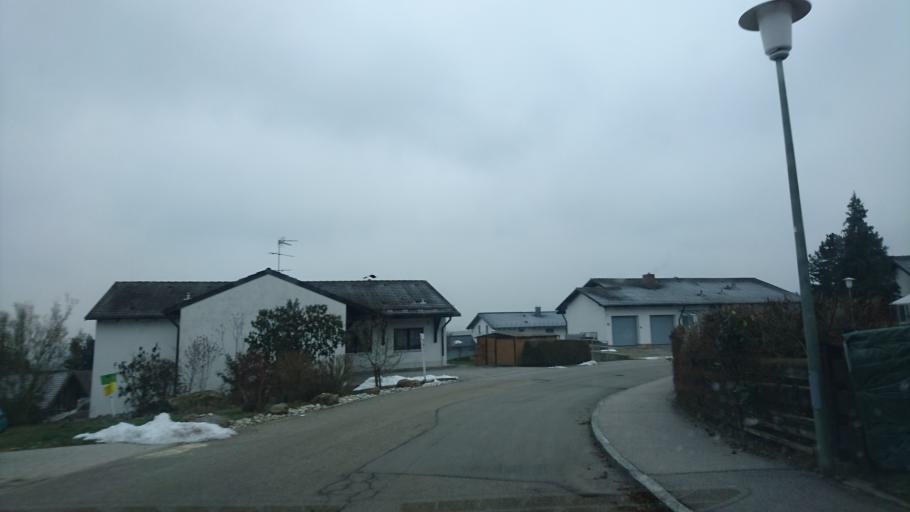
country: DE
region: Bavaria
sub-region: Lower Bavaria
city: Bad Griesbach
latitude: 48.4397
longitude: 13.1940
